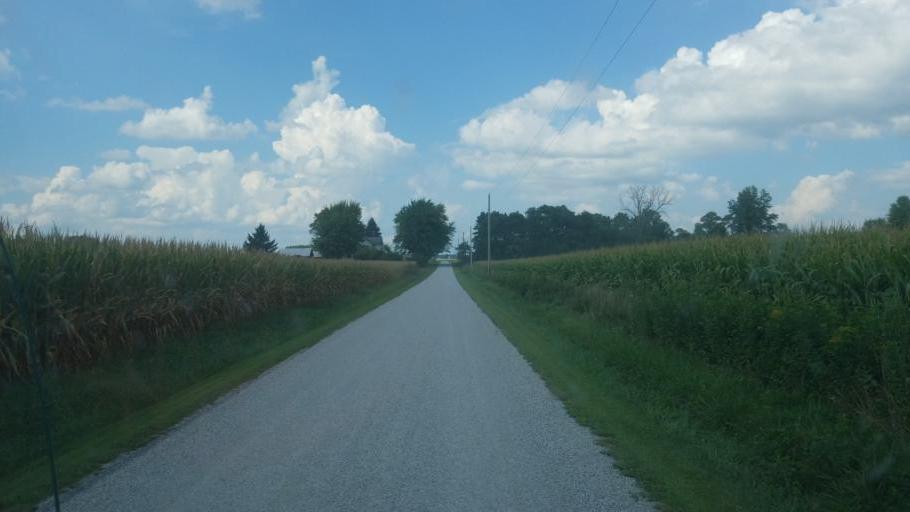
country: US
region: Ohio
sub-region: Huron County
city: Willard
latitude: 40.9915
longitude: -82.7965
